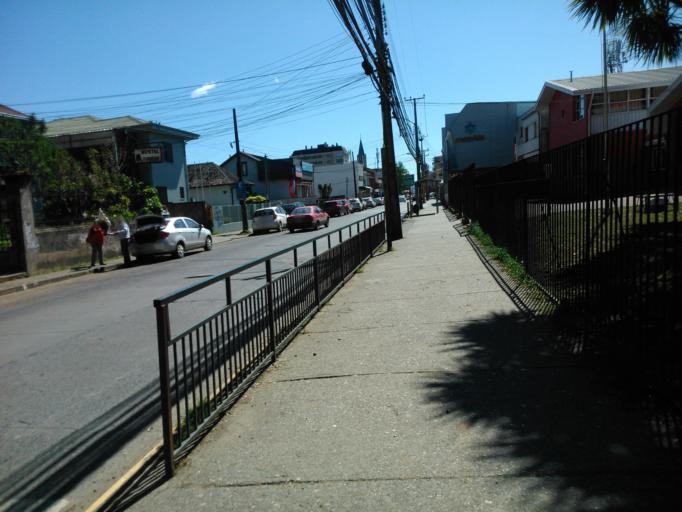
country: CL
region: Los Rios
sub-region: Provincia de Valdivia
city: Valdivia
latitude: -39.8178
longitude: -73.2472
